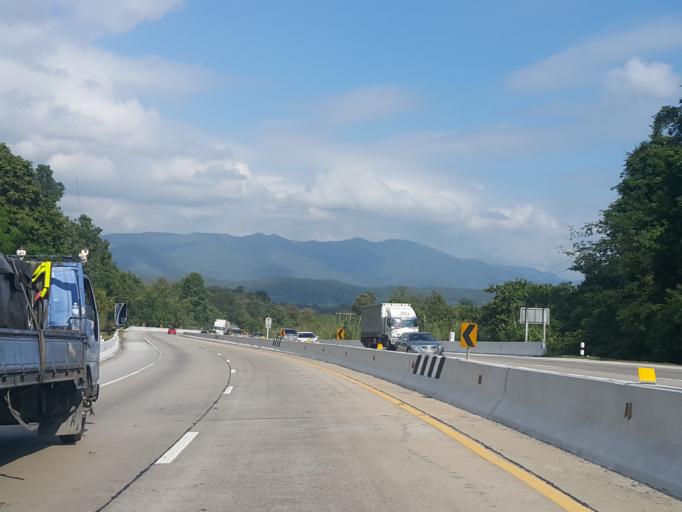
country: TH
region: Lamphun
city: Mae Tha
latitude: 18.4392
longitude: 99.2052
